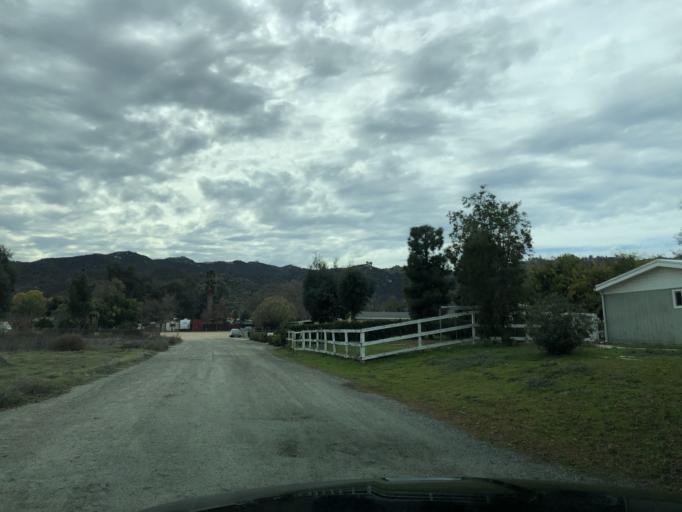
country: US
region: California
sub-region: Riverside County
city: Wildomar
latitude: 33.6035
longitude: -117.2801
